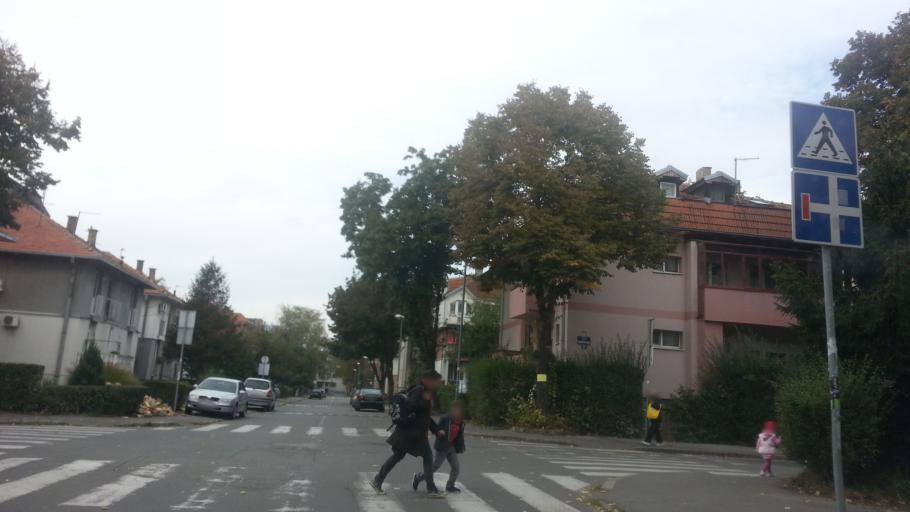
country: RS
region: Central Serbia
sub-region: Belgrade
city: Zemun
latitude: 44.8568
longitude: 20.3682
